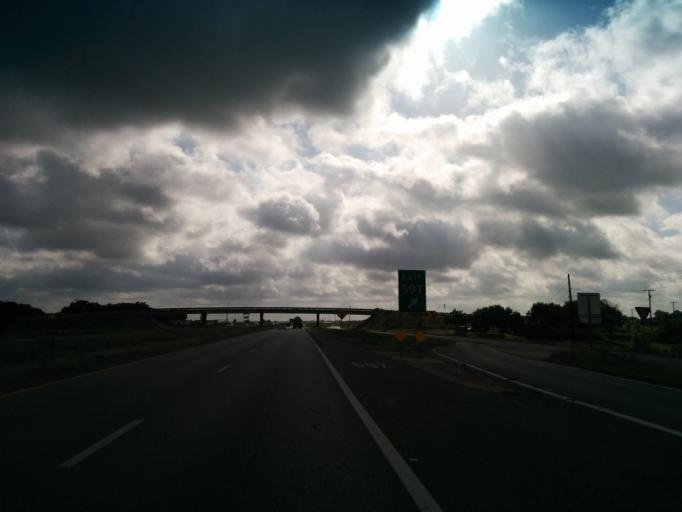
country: US
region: Texas
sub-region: Guadalupe County
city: Marion
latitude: 29.5181
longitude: -98.1409
